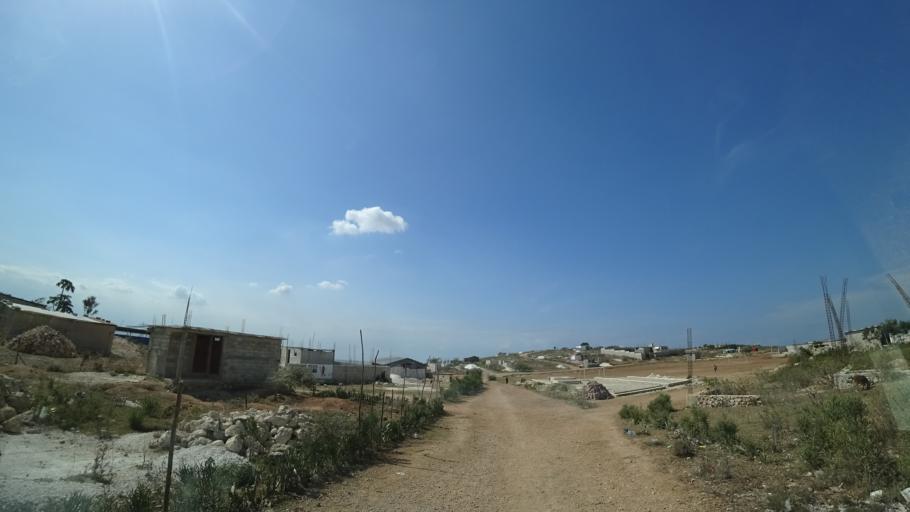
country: HT
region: Ouest
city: Croix des Bouquets
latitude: 18.6732
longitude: -72.2995
